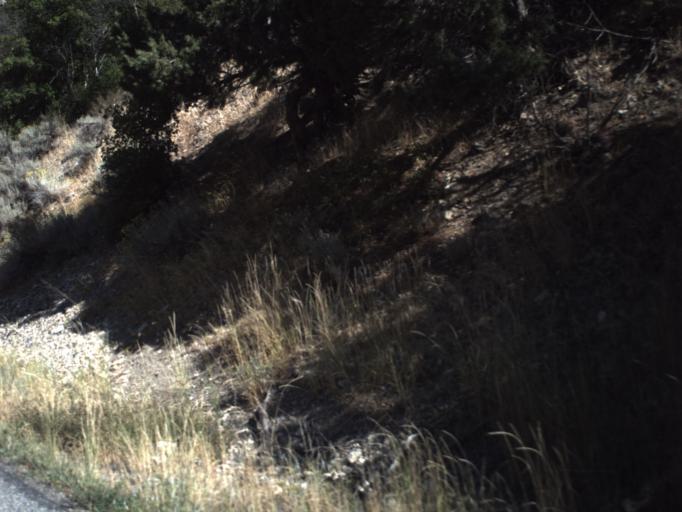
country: US
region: Utah
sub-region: Cache County
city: Hyrum
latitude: 41.6225
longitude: -111.7829
